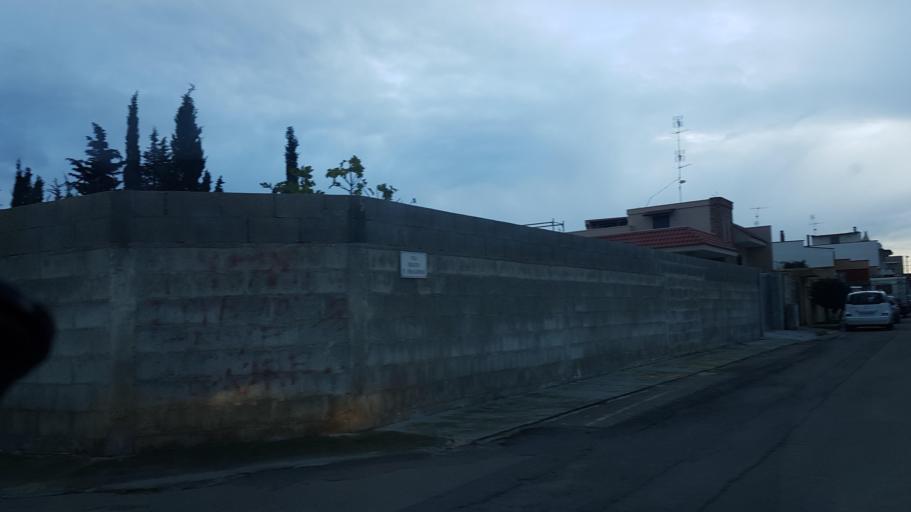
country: IT
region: Apulia
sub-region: Provincia di Lecce
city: Merine
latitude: 40.3365
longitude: 18.2186
